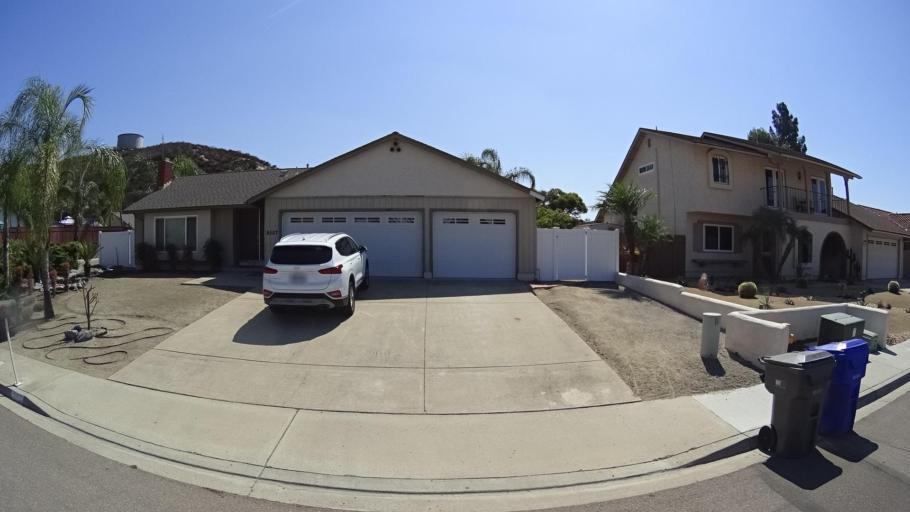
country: US
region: California
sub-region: San Diego County
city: Winter Gardens
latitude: 32.8312
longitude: -116.9195
